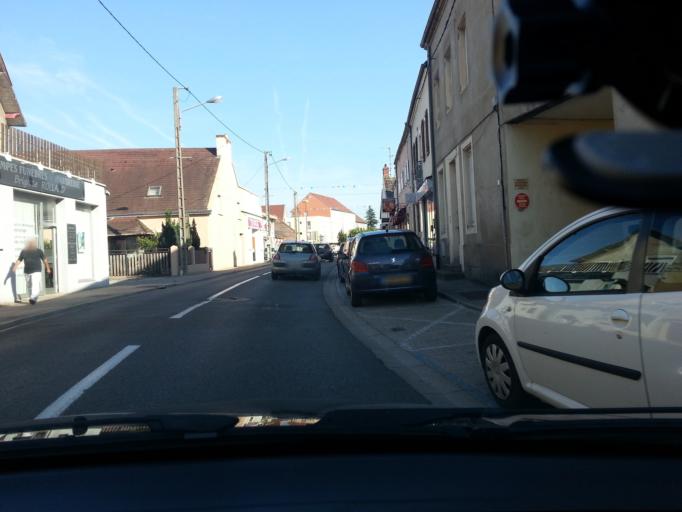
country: FR
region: Bourgogne
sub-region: Departement de Saone-et-Loire
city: Saint-Marcel
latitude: 46.7752
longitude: 4.8912
